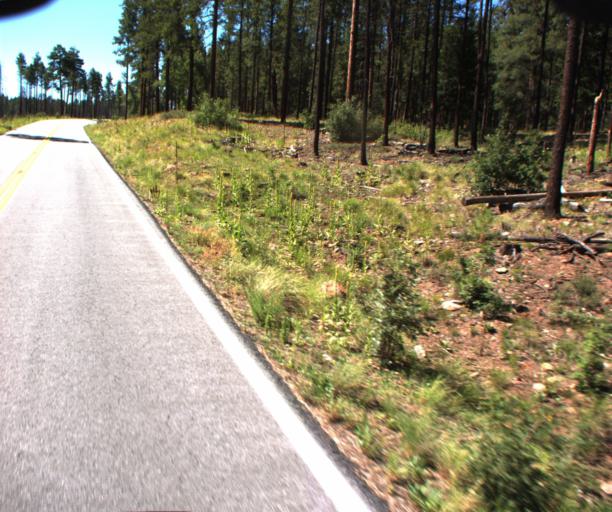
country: US
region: Arizona
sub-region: Apache County
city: Eagar
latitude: 33.7095
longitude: -109.2027
